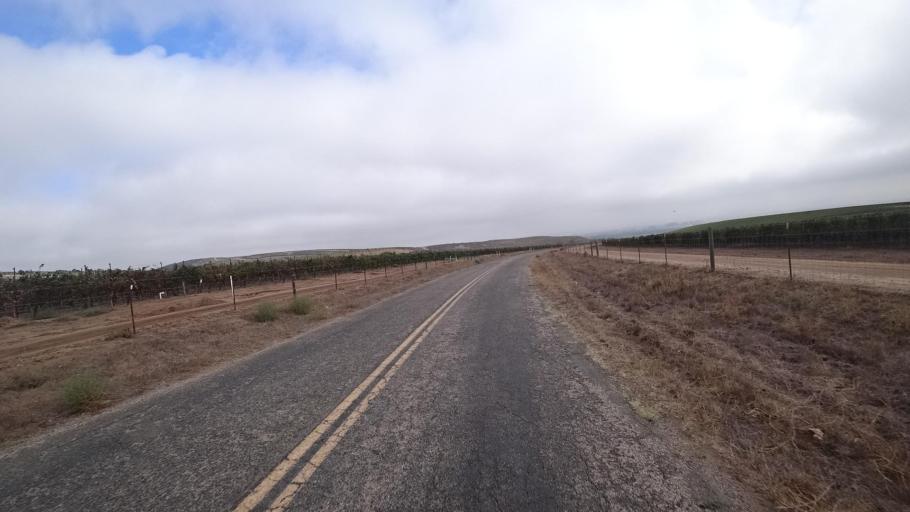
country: US
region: California
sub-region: Monterey County
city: Soledad
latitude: 36.3442
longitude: -121.3409
